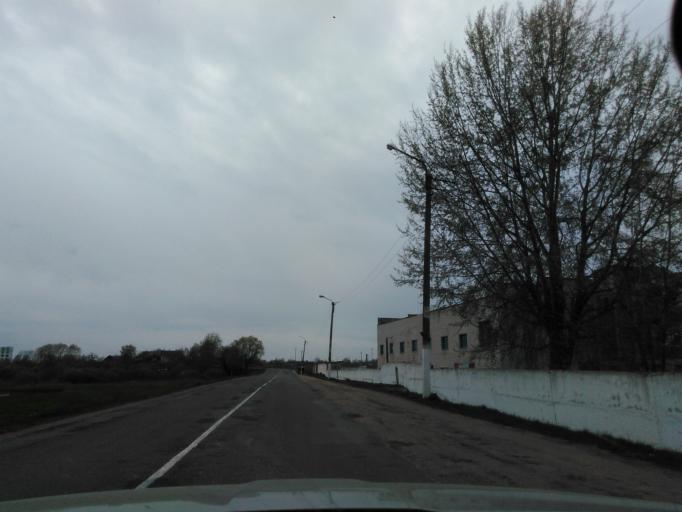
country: BY
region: Vitebsk
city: Chashniki
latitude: 54.8428
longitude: 29.1931
